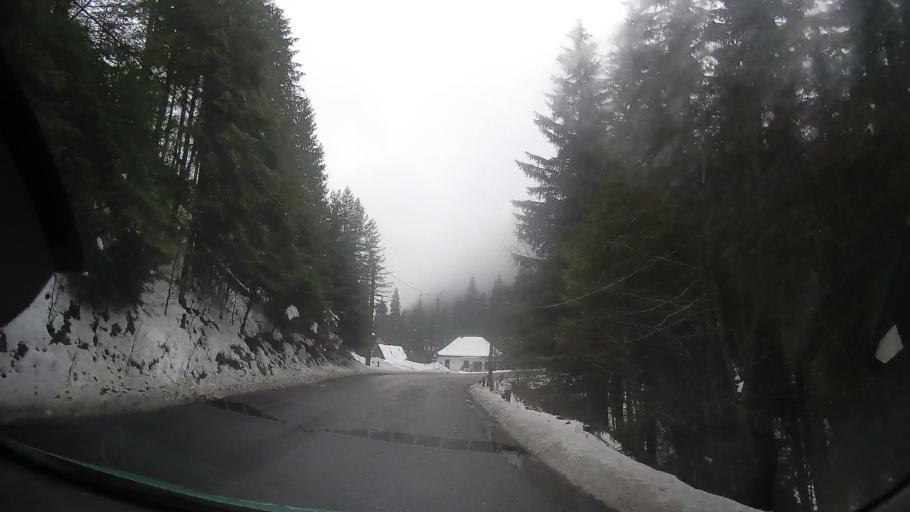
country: RO
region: Neamt
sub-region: Comuna Bicaz Chei
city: Bicaz Chei
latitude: 46.7808
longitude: 25.7855
